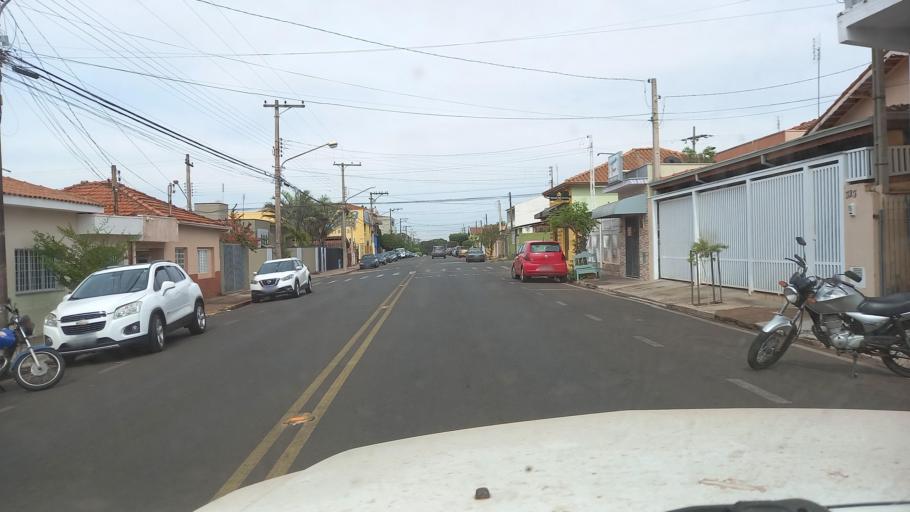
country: BR
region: Sao Paulo
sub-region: Moji-Guacu
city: Mogi-Gaucu
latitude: -22.3597
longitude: -46.9419
